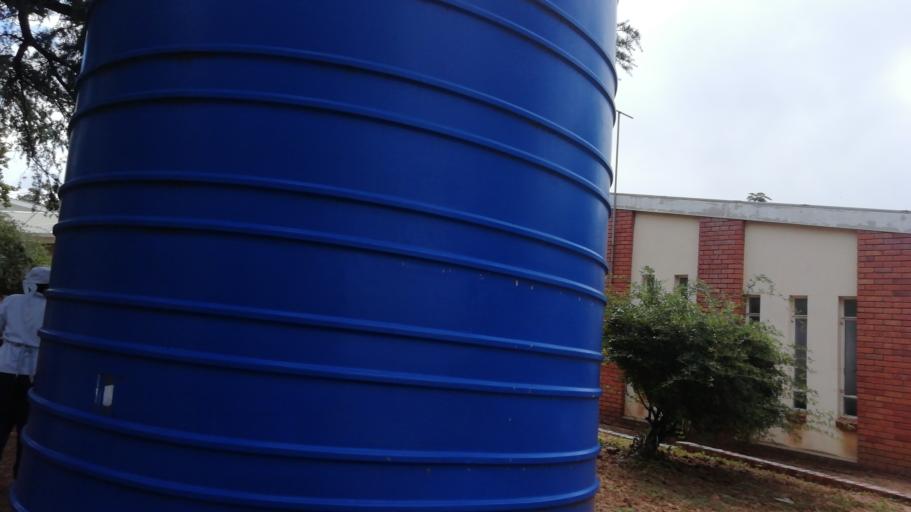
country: LS
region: Maseru
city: Nako
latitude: -29.6310
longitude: 27.5013
